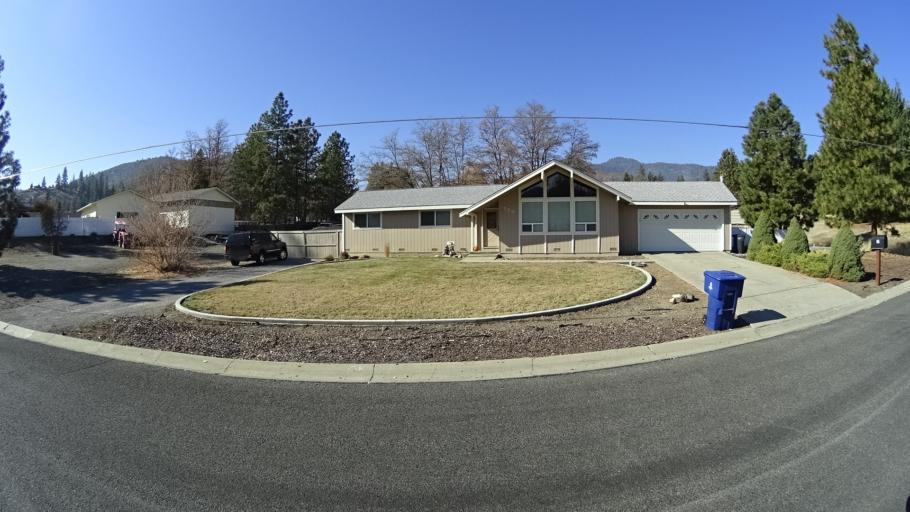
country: US
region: California
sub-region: Siskiyou County
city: Yreka
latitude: 41.7325
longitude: -122.6510
